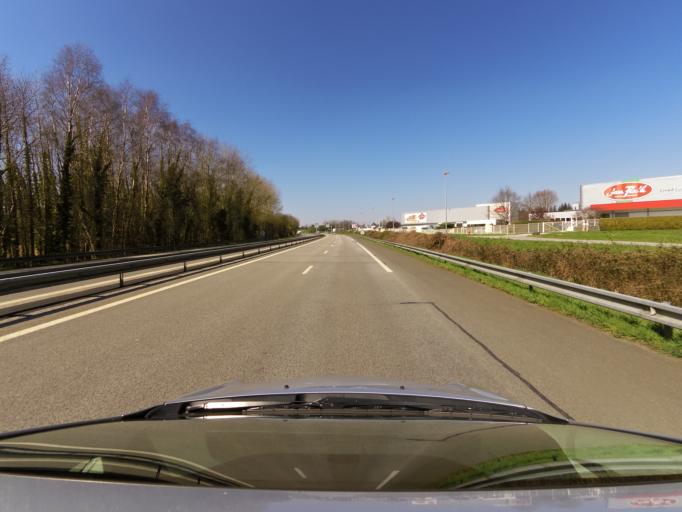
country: FR
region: Brittany
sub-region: Departement du Morbihan
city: Baud
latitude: 47.8944
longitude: -3.0055
